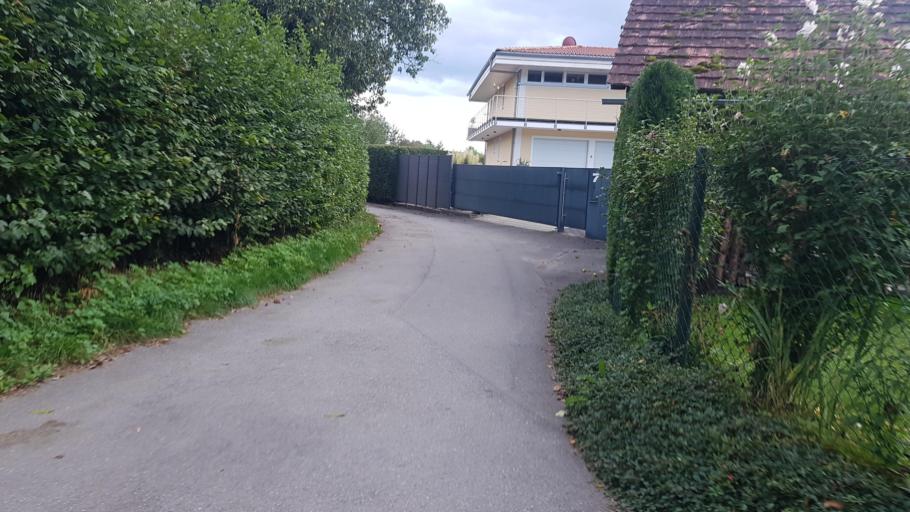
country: DE
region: Baden-Wuerttemberg
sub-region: Tuebingen Region
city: Friedrichshafen
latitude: 47.6583
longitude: 9.4399
